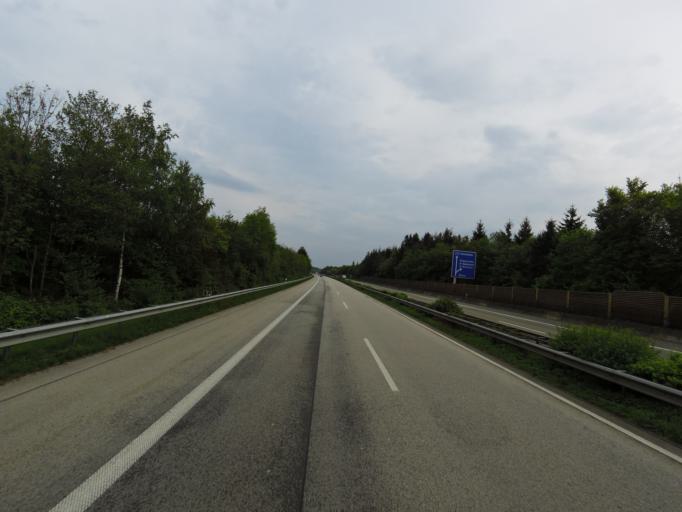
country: DE
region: Rheinland-Pfalz
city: Kratzenburg
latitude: 50.2172
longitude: 7.5424
